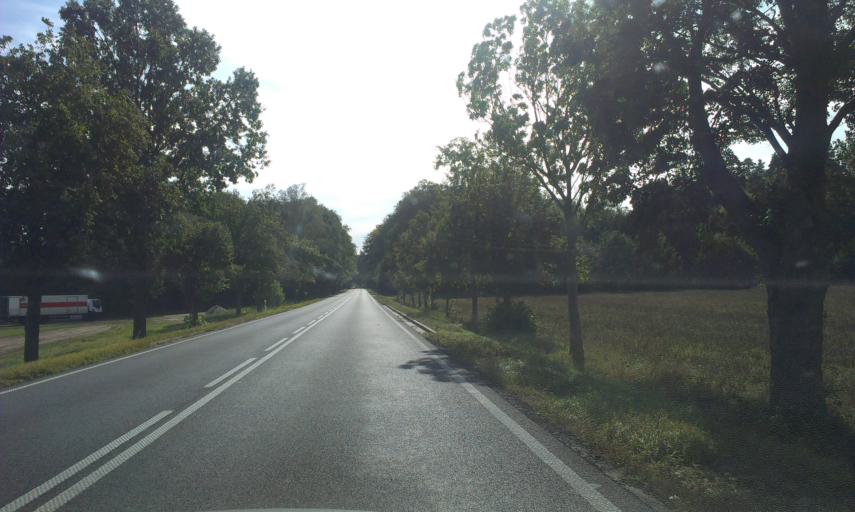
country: PL
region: West Pomeranian Voivodeship
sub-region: Powiat szczecinecki
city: Szczecinek
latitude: 53.6399
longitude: 16.7609
